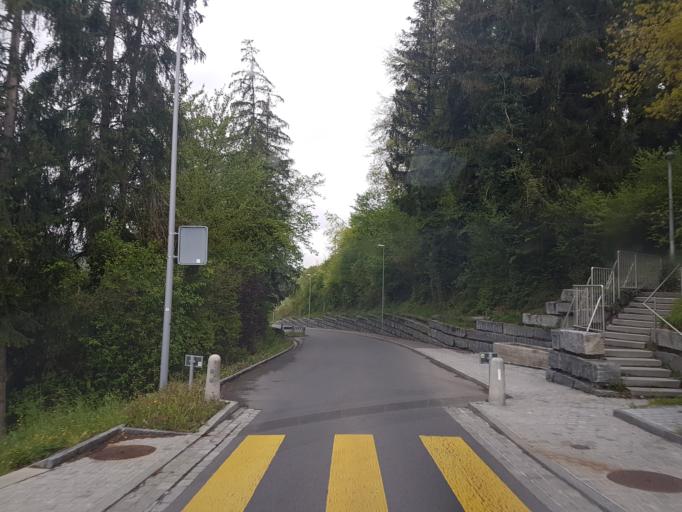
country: CH
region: Zurich
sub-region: Bezirk Dietikon
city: Birmensdorf
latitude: 47.3581
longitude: 8.4455
